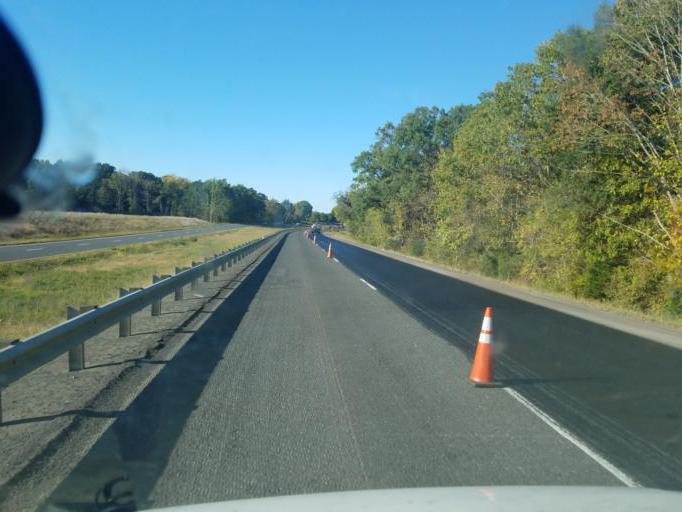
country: US
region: Virginia
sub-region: Fauquier County
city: Bealeton
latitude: 38.5201
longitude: -77.8354
